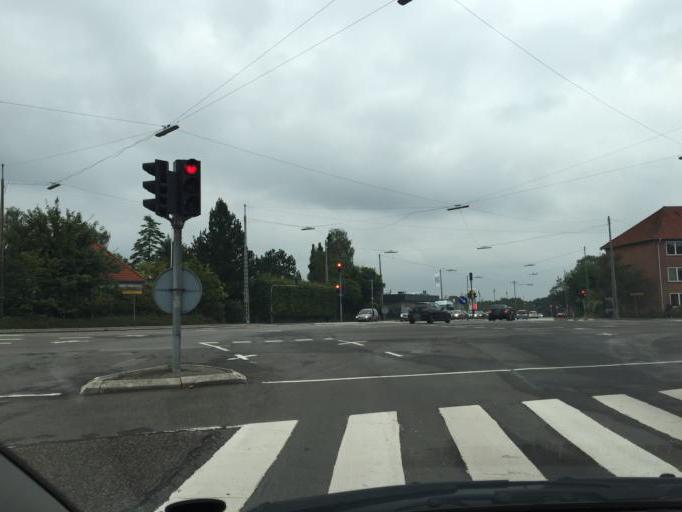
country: DK
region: Capital Region
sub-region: Herlev Kommune
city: Herlev
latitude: 55.7287
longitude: 12.4370
